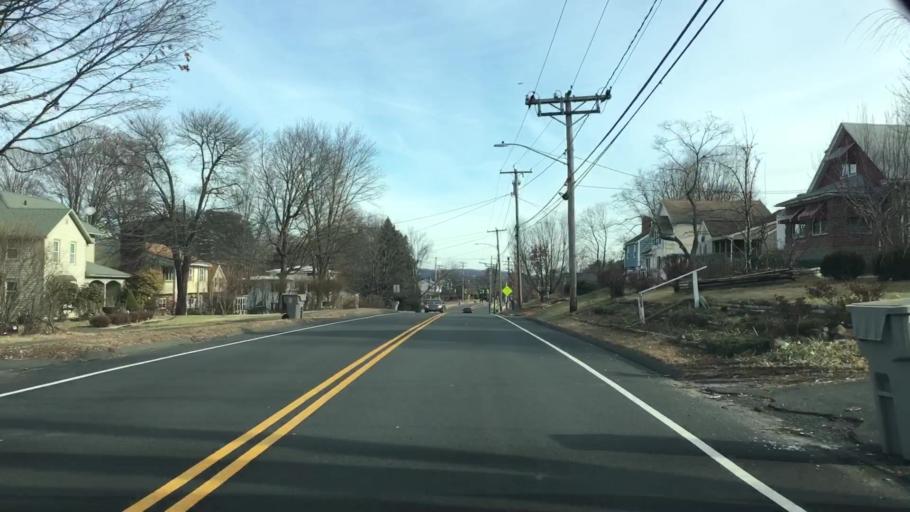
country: US
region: Connecticut
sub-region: Hartford County
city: Plainville
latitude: 41.6686
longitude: -72.9000
